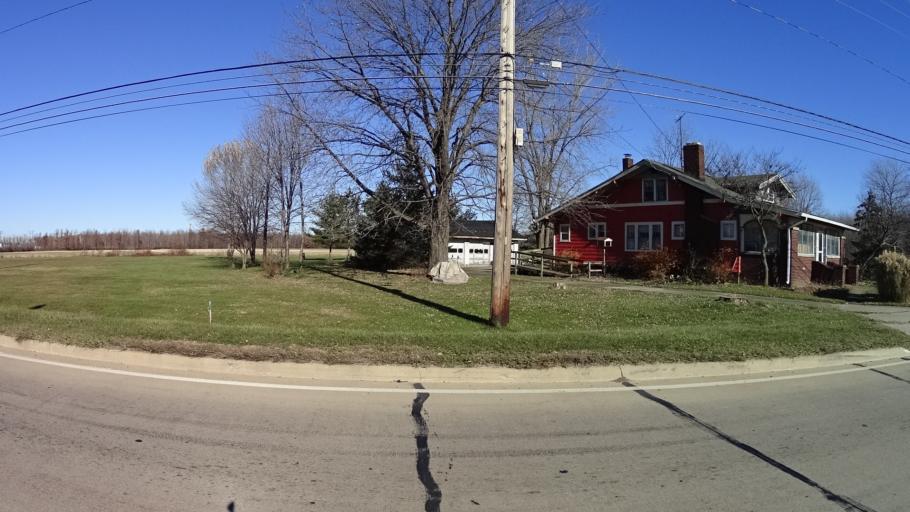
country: US
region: Ohio
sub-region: Lorain County
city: Avon
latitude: 41.4672
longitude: -82.0627
